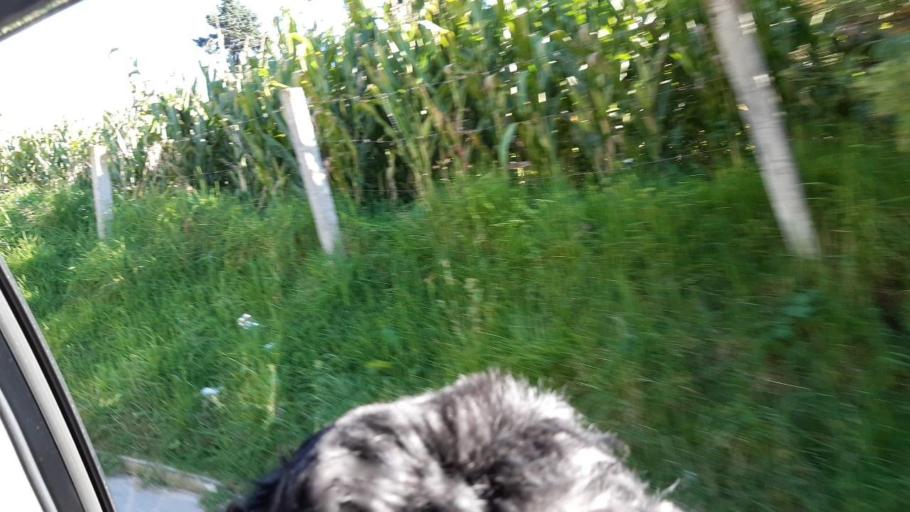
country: GT
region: Quetzaltenango
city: Salcaja
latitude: 14.8773
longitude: -91.4524
